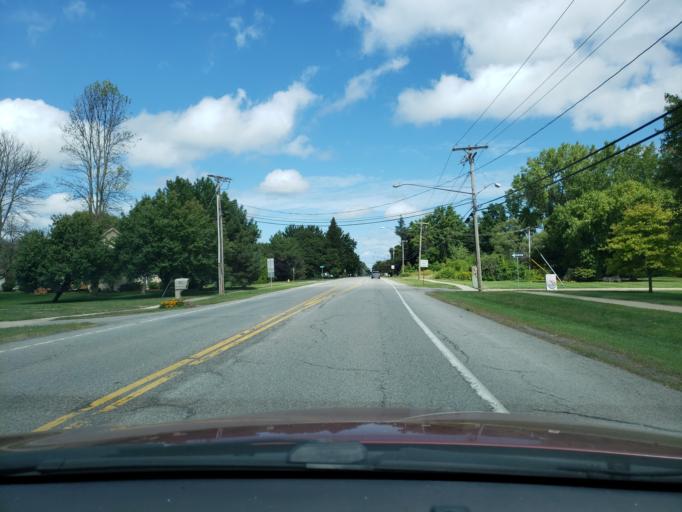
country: US
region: New York
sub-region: Monroe County
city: Greece
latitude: 43.2276
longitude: -77.7336
